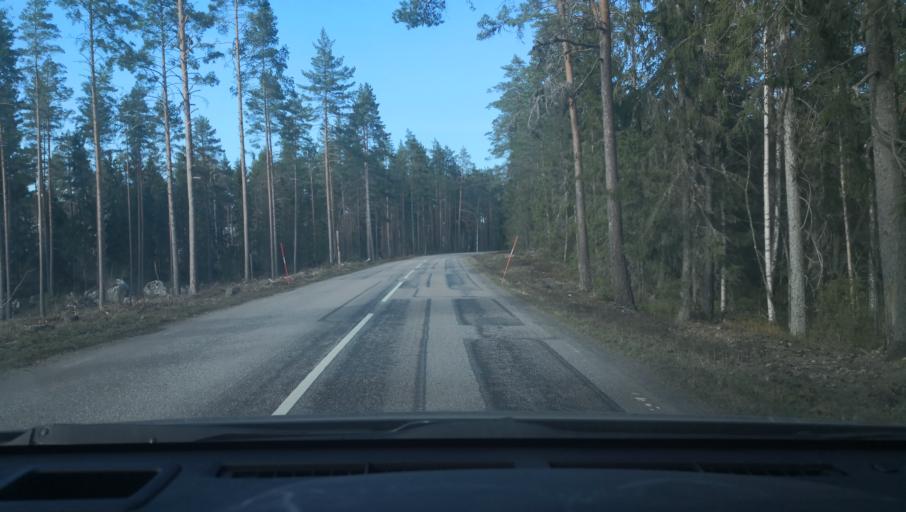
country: SE
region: Uppsala
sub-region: Heby Kommun
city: Morgongava
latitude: 60.0029
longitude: 16.9316
